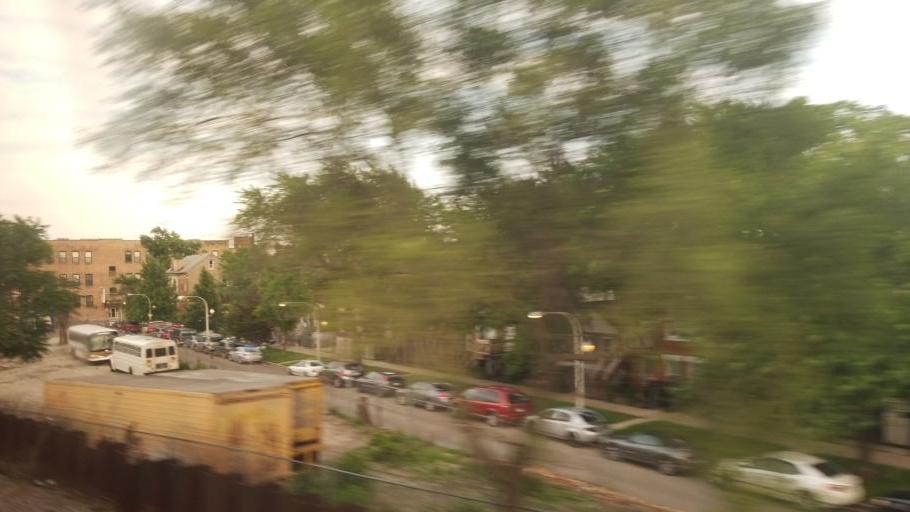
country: US
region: Illinois
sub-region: Cook County
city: Chicago
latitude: 41.8548
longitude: -87.6973
